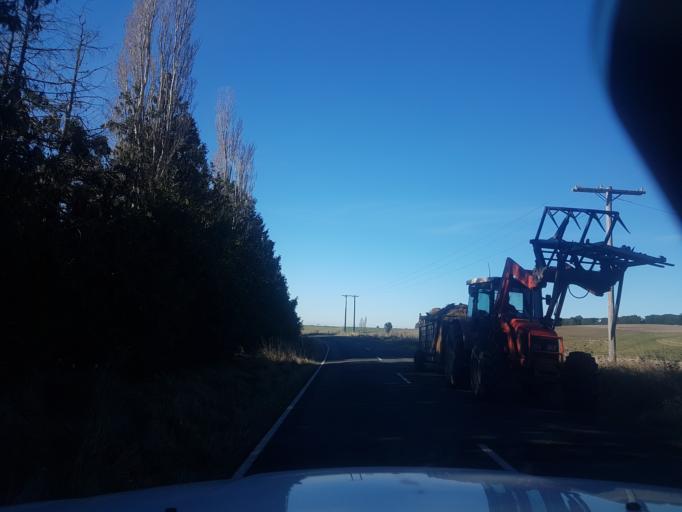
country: NZ
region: Canterbury
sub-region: Timaru District
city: Pleasant Point
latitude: -44.2754
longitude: 171.1215
